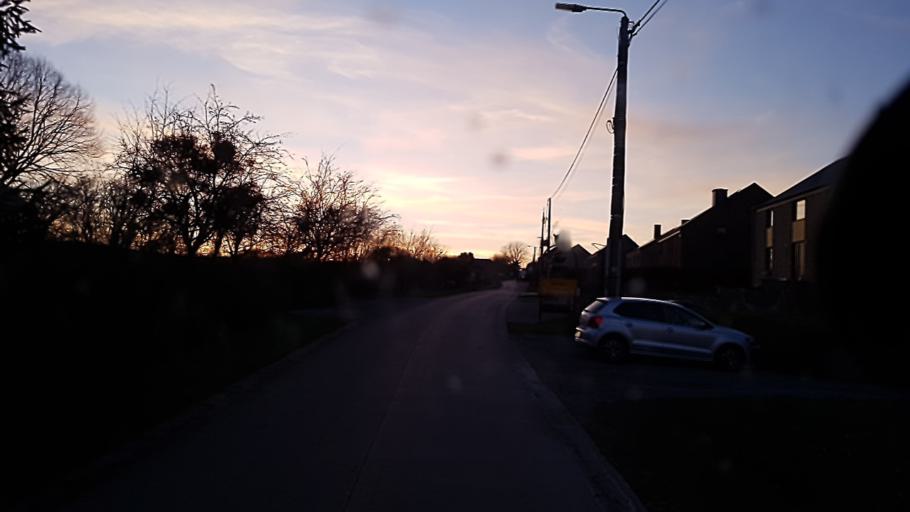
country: BE
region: Wallonia
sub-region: Province du Luxembourg
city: Wellin
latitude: 50.0679
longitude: 5.0776
